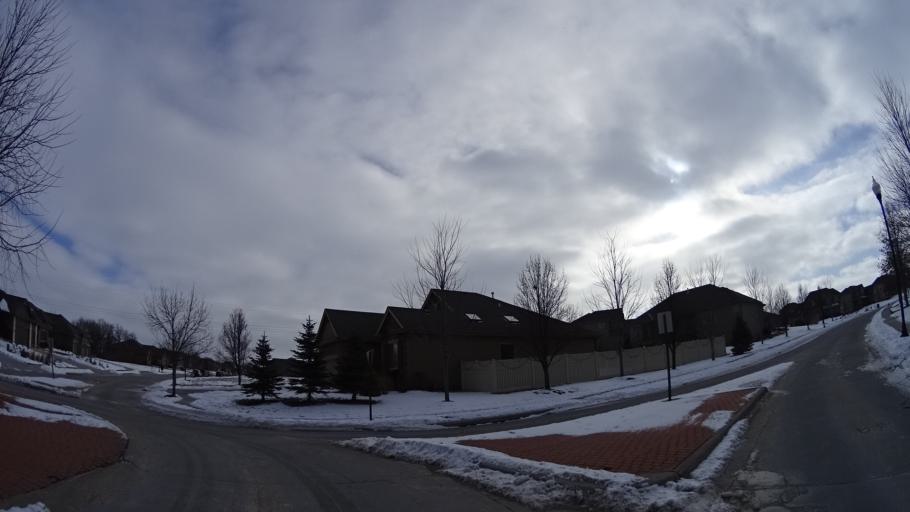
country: US
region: Nebraska
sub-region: Sarpy County
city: Papillion
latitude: 41.1269
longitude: -96.0269
